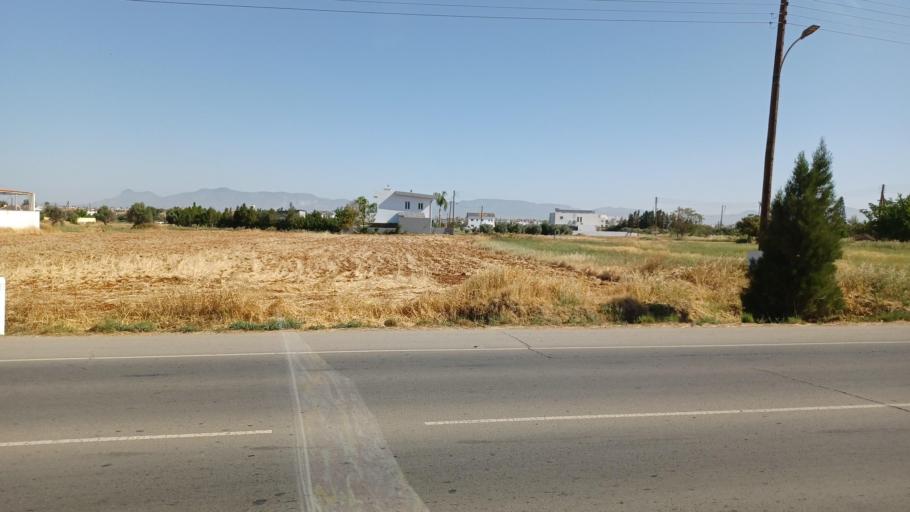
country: CY
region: Lefkosia
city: Kokkinotrimithia
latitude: 35.1487
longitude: 33.2111
